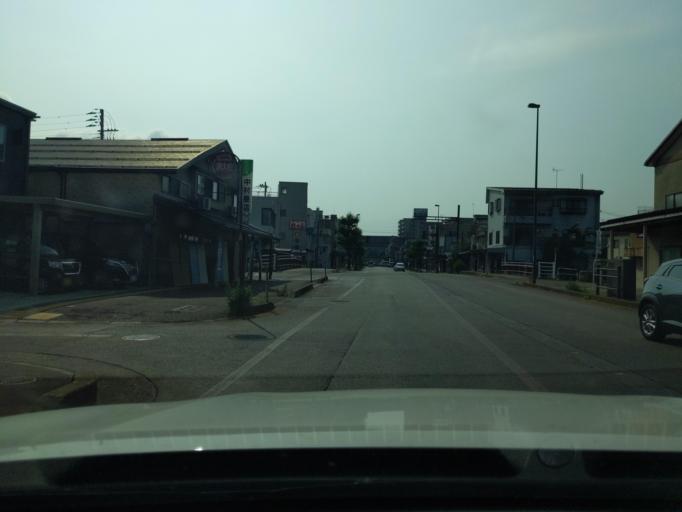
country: JP
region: Niigata
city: Nagaoka
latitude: 37.4417
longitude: 138.8553
